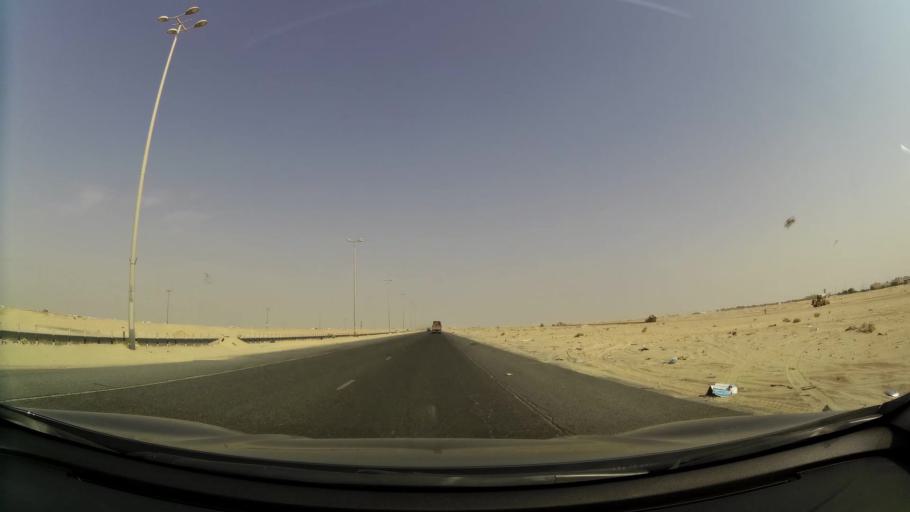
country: KW
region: Al Ahmadi
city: Al Wafrah
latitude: 28.8103
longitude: 48.0428
